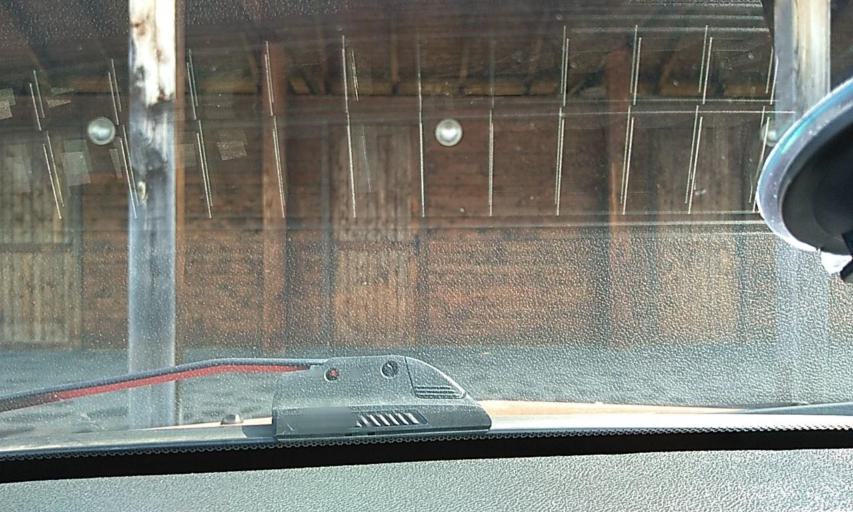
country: RO
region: Brasov
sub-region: Oras Rupea
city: Rupea
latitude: 46.0382
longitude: 25.2117
